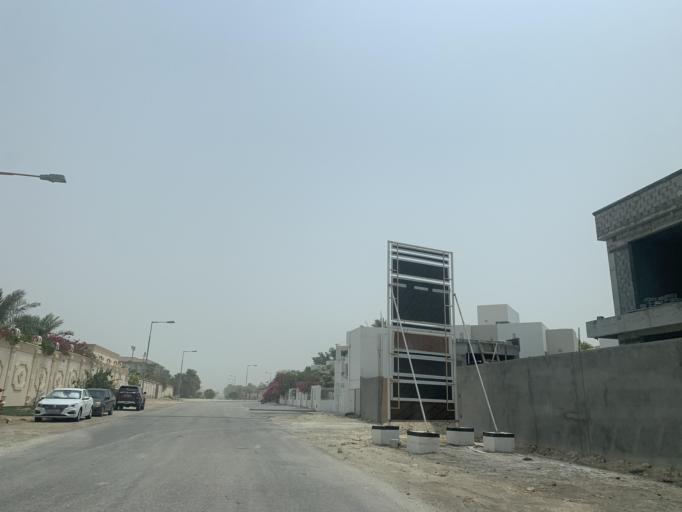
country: BH
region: Central Governorate
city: Madinat Hamad
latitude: 26.1652
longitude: 50.4766
